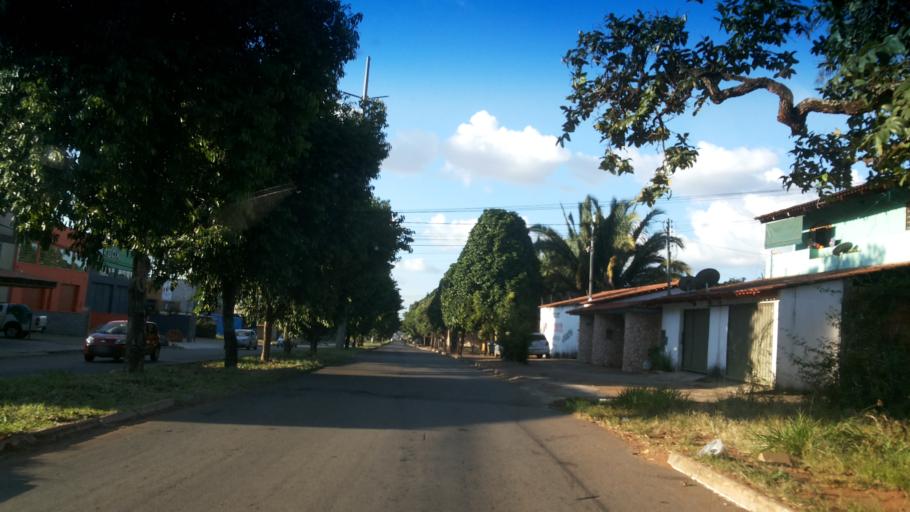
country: BR
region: Goias
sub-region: Goiania
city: Goiania
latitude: -16.7348
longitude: -49.3097
